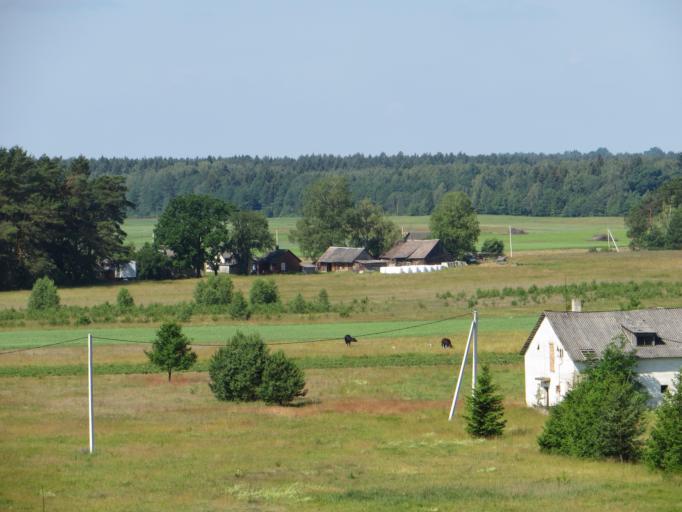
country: LT
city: Prienai
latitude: 54.5512
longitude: 23.9556
